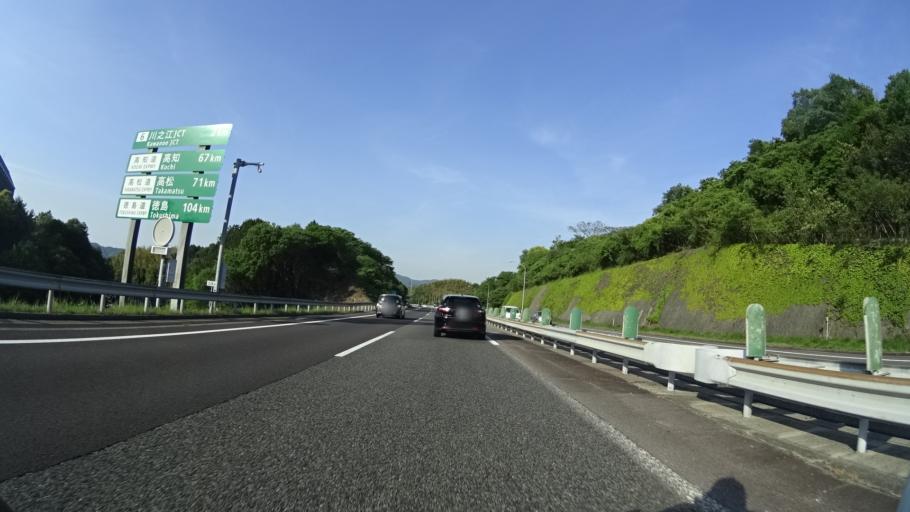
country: JP
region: Ehime
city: Kawanoecho
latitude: 33.9818
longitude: 133.5835
